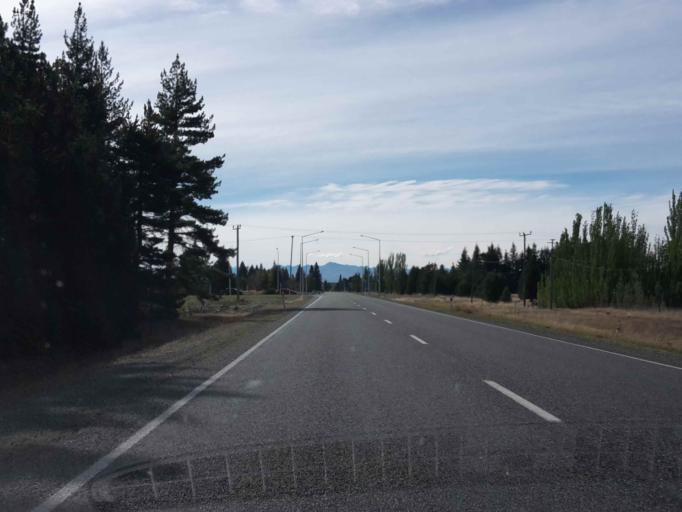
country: NZ
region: Canterbury
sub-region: Timaru District
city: Pleasant Point
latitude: -44.2661
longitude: 170.1025
